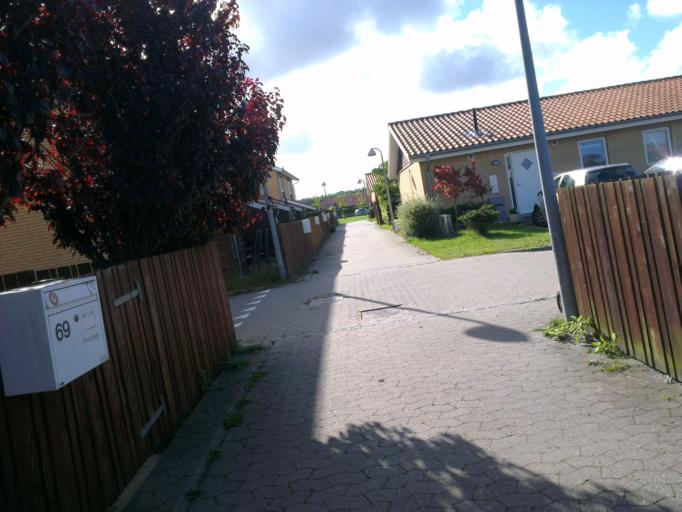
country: DK
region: Capital Region
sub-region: Frederikssund Kommune
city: Slangerup
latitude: 55.8401
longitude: 12.1684
